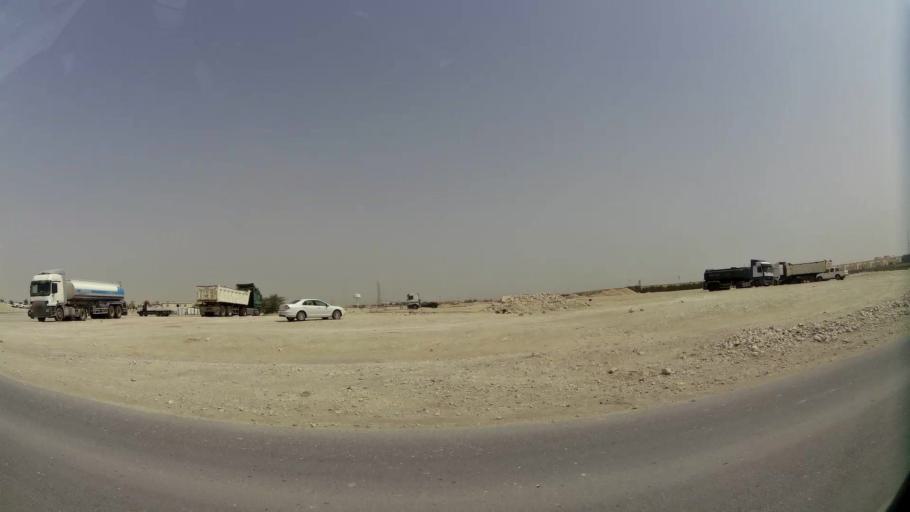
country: QA
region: Baladiyat ar Rayyan
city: Ar Rayyan
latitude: 25.2346
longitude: 51.4060
